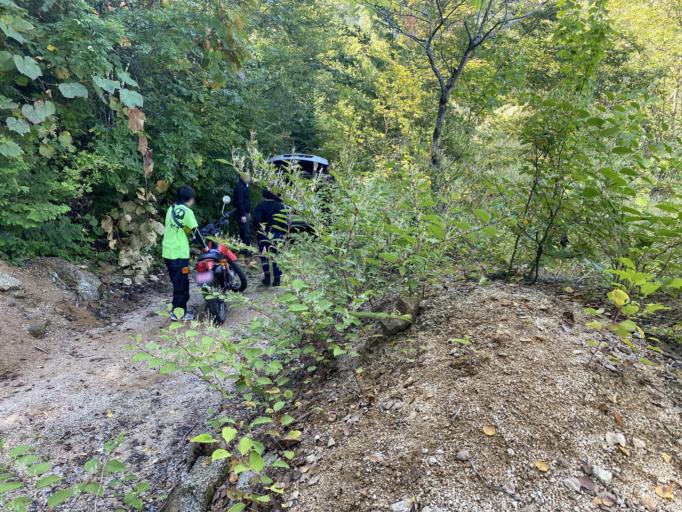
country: JP
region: Nagano
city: Omachi
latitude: 36.5000
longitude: 137.7967
